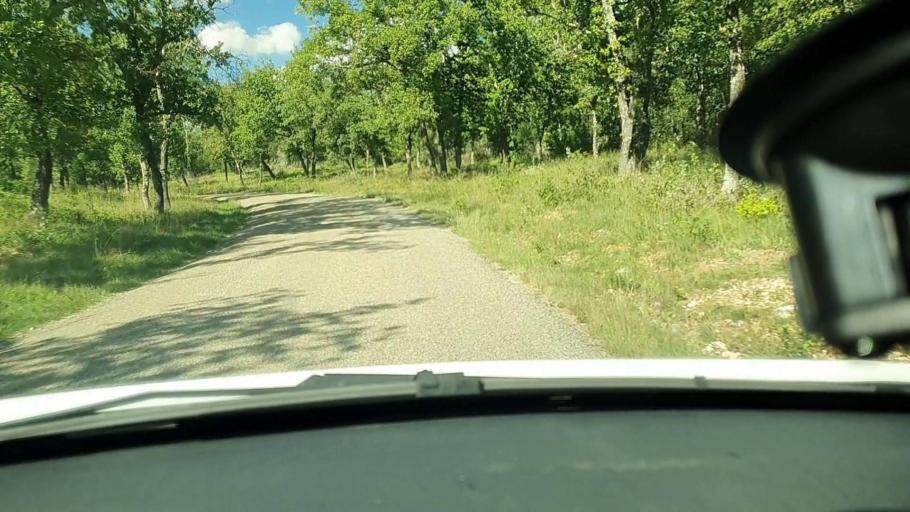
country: FR
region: Languedoc-Roussillon
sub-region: Departement du Gard
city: Goudargues
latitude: 44.1586
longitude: 4.4089
